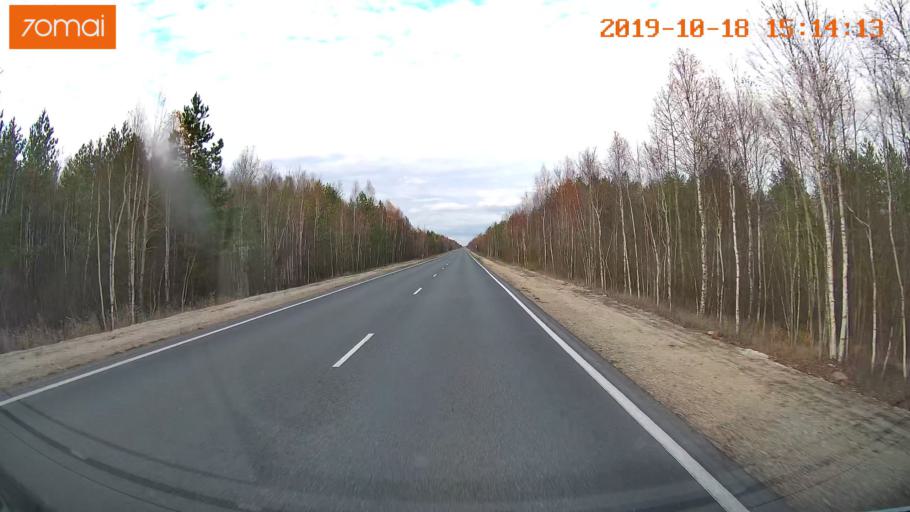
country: RU
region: Vladimir
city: Gus'-Khrustal'nyy
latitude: 55.5990
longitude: 40.7198
